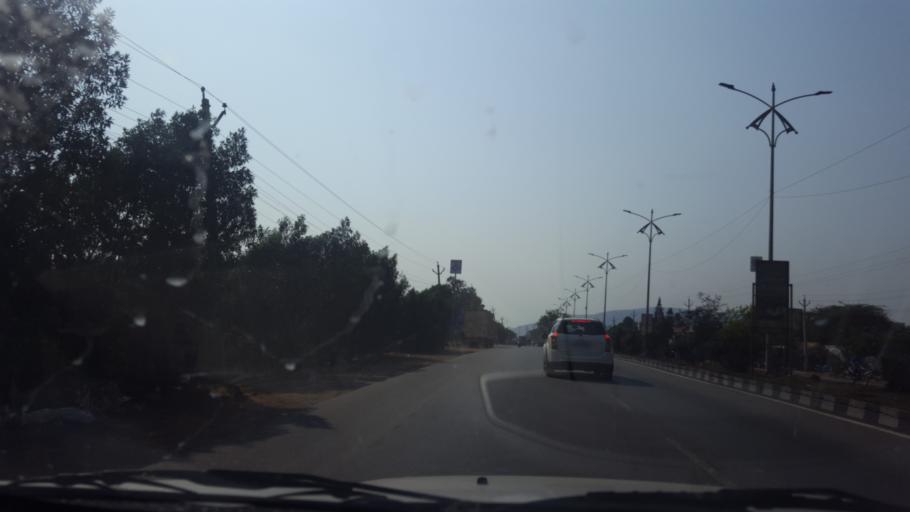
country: IN
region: Andhra Pradesh
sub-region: Vishakhapatnam
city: Visakhapatnam
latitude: 17.6891
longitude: 83.1048
